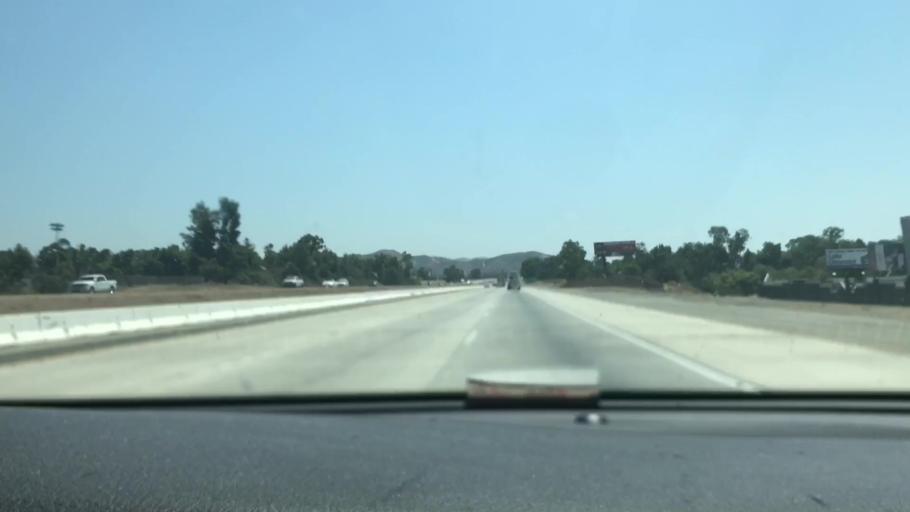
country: US
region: California
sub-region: Riverside County
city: Lake Elsinore
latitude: 33.7014
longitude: -117.3501
